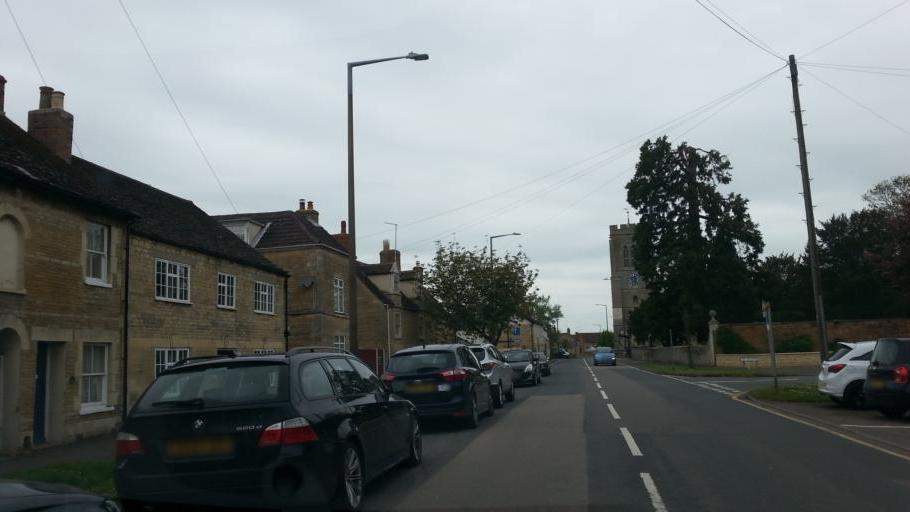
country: GB
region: England
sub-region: Lincolnshire
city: Market Deeping
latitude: 52.6774
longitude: -0.3191
